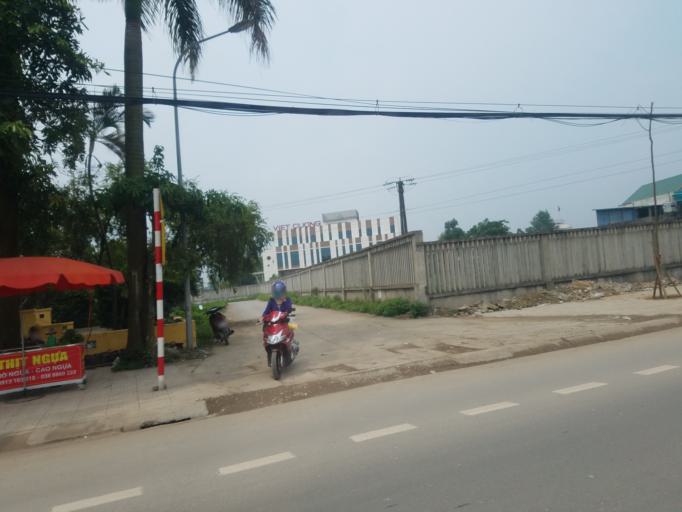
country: VN
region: Thai Nguyen
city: Chua Hang
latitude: 21.6087
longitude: 105.8397
